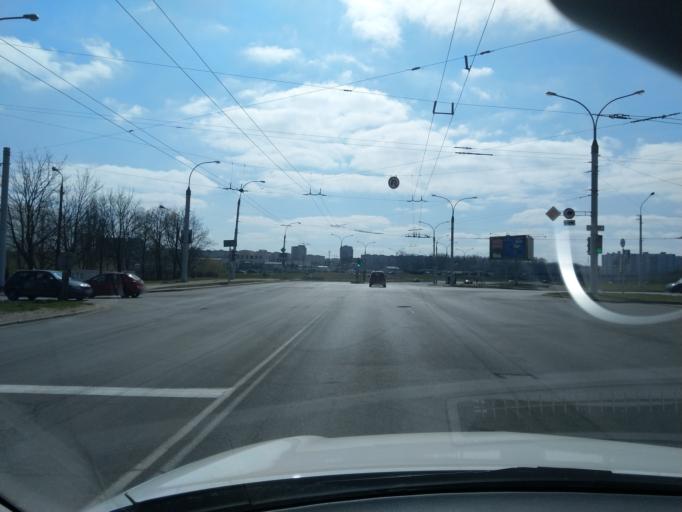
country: BY
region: Minsk
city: Syenitsa
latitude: 53.8582
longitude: 27.4979
